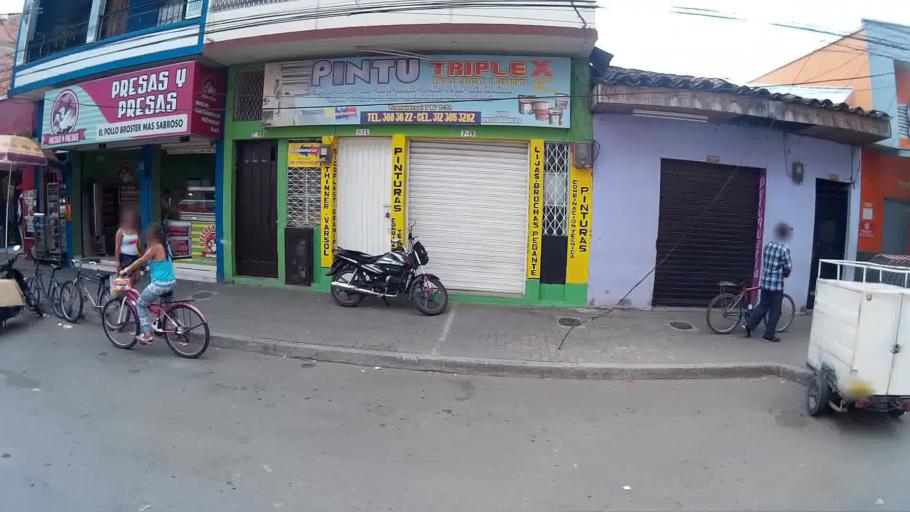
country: CO
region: Risaralda
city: La Virginia
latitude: 4.8956
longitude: -75.8841
